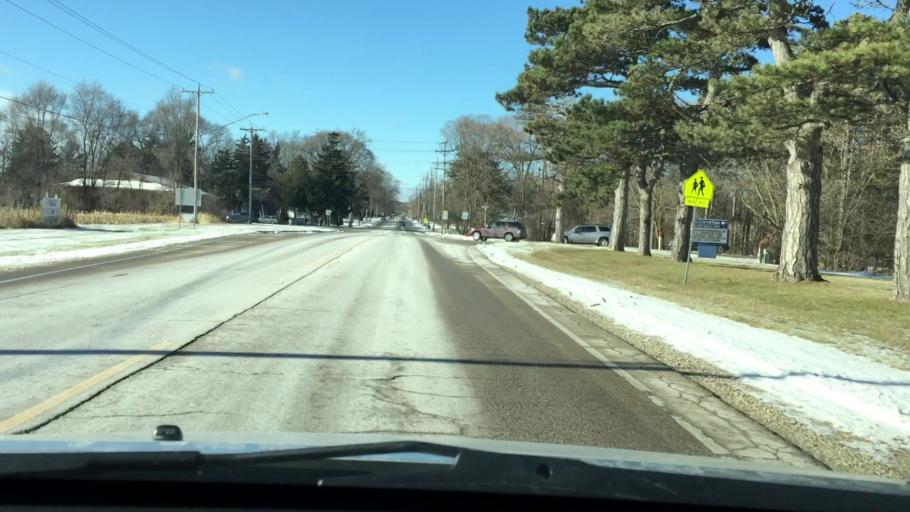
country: US
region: Wisconsin
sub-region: Waukesha County
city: Eagle
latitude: 42.8790
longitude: -88.4619
